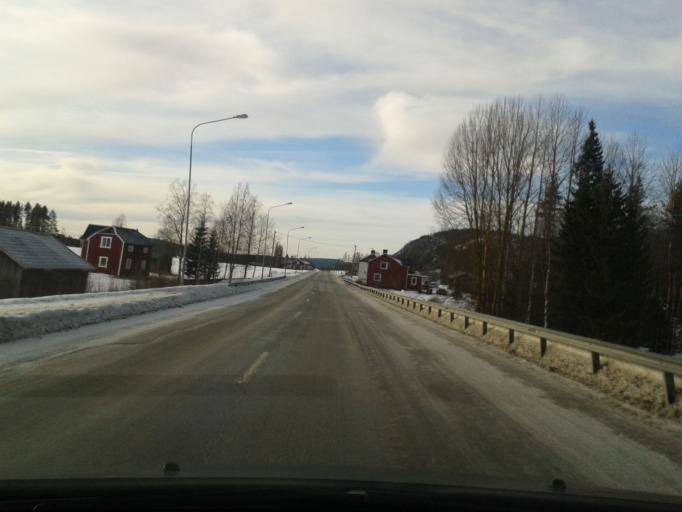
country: SE
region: Vaesternorrland
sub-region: OErnskoeldsviks Kommun
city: Bredbyn
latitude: 63.5261
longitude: 18.0394
